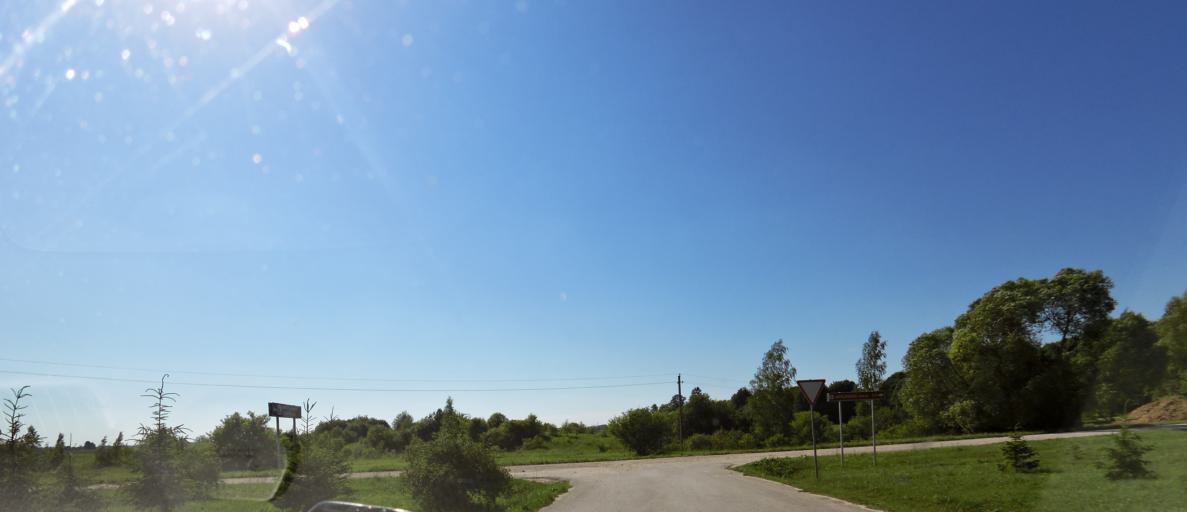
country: LT
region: Panevezys
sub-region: Birzai
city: Birzai
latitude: 56.2060
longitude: 24.6925
